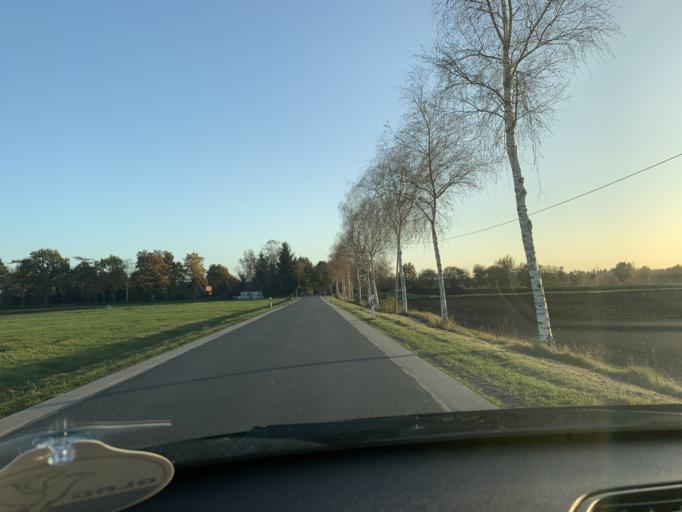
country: DE
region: Lower Saxony
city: Bad Zwischenahn
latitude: 53.1466
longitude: 8.0526
